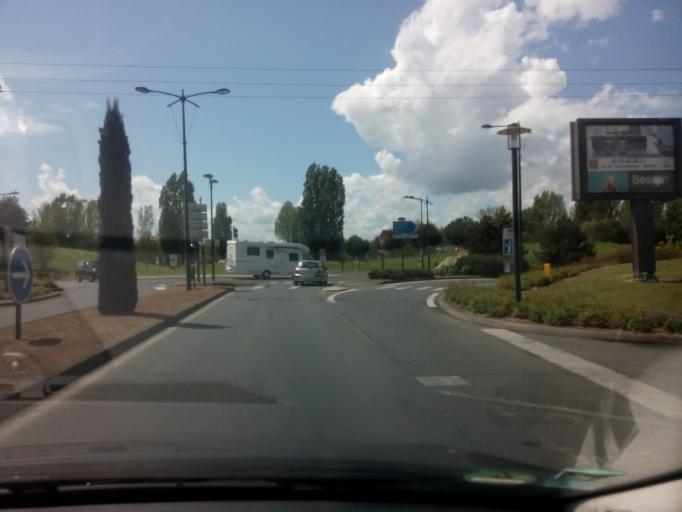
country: FR
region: Limousin
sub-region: Departement de la Correze
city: Saint-Pantaleon-de-Larche
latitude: 45.1477
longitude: 1.4871
